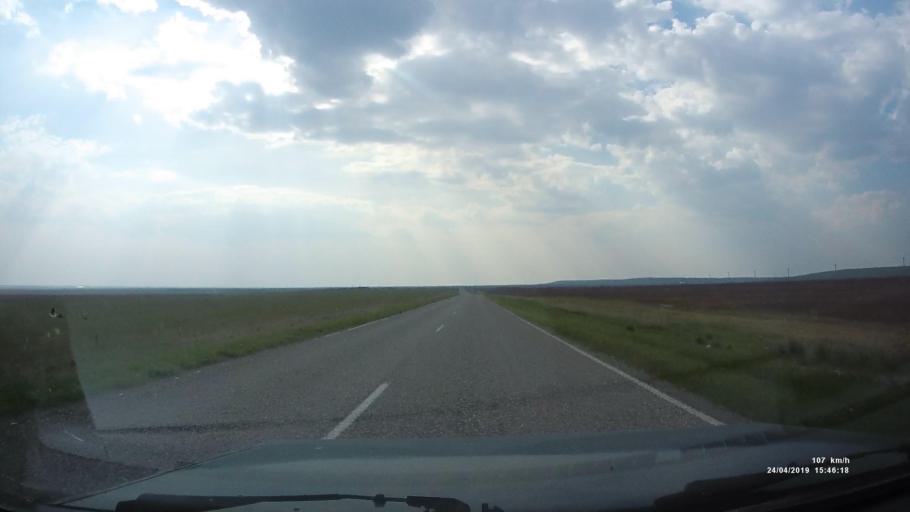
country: RU
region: Kalmykiya
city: Yashalta
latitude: 46.5927
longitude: 42.7180
